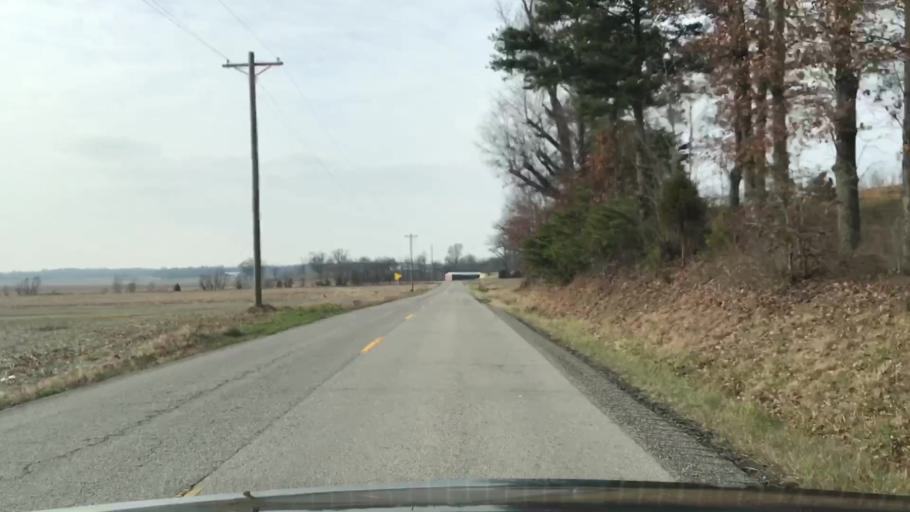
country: US
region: Kentucky
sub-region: Webster County
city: Sebree
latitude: 37.5147
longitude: -87.4082
